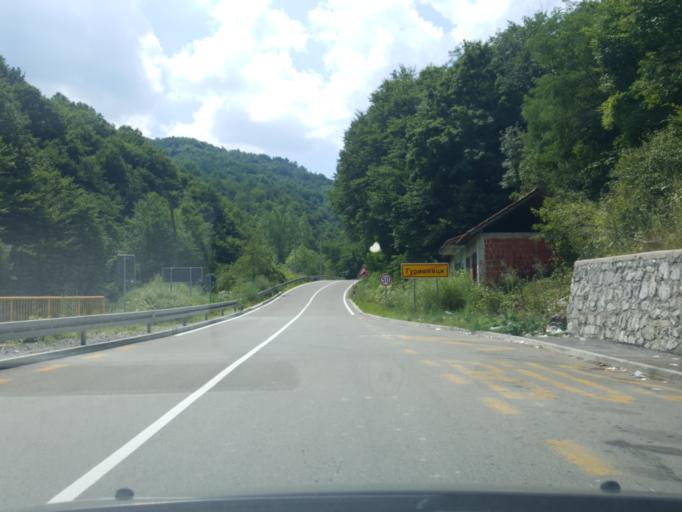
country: RS
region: Central Serbia
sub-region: Sumadijski Okrug
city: Arangelovac
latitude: 44.1661
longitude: 20.5143
